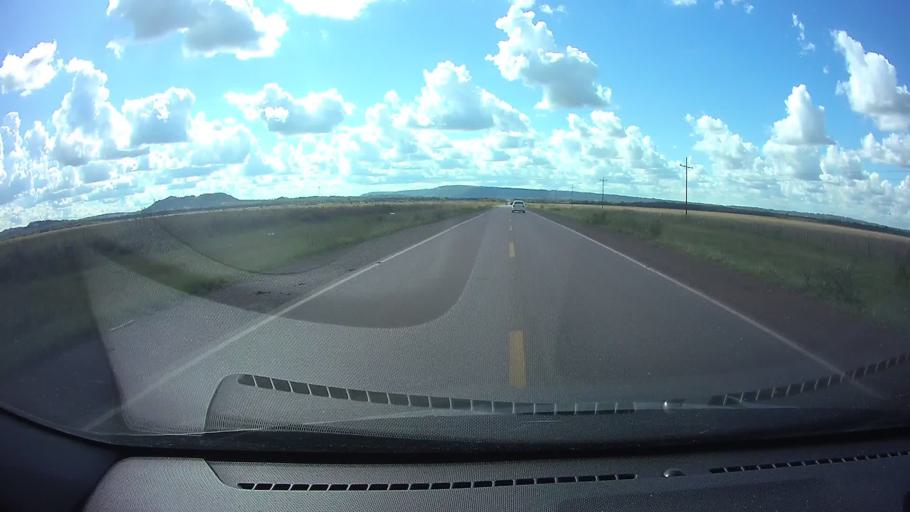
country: PY
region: Paraguari
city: Sapucai
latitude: -25.7362
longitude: -56.8152
